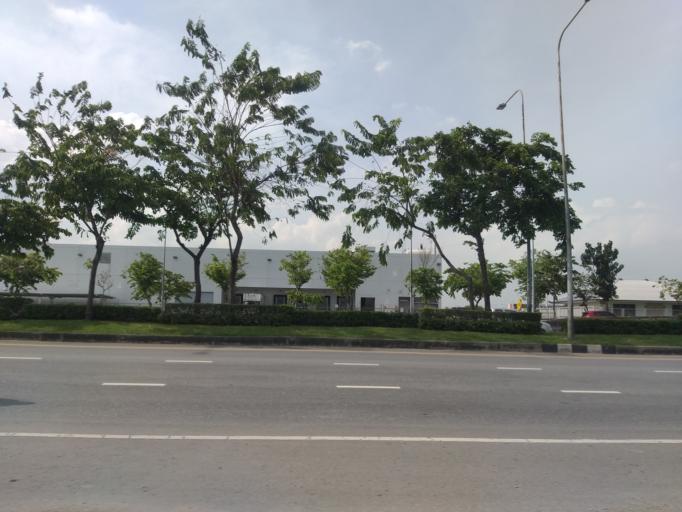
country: TH
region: Bangkok
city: Lat Krabang
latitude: 13.7106
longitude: 100.7649
